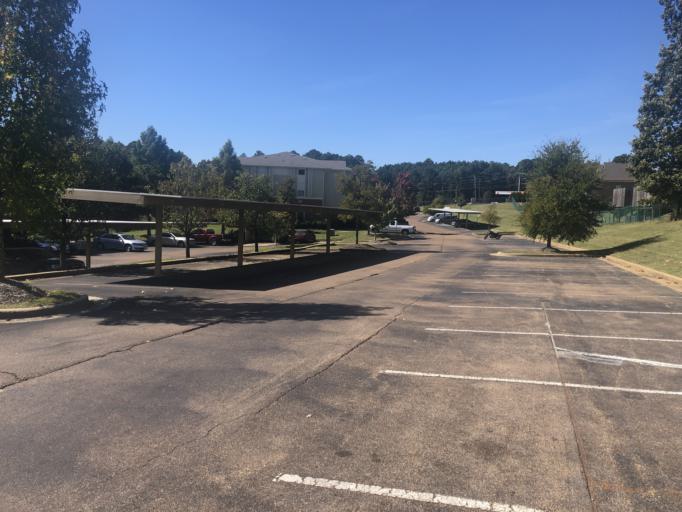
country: US
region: Mississippi
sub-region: Lafayette County
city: University
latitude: 34.3463
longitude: -89.5411
